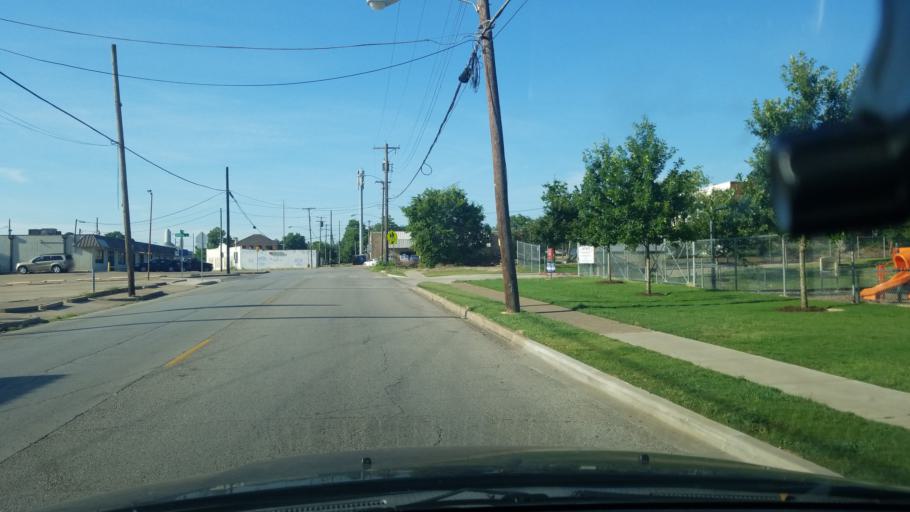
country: US
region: Texas
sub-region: Dallas County
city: Dallas
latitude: 32.7283
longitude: -96.8114
